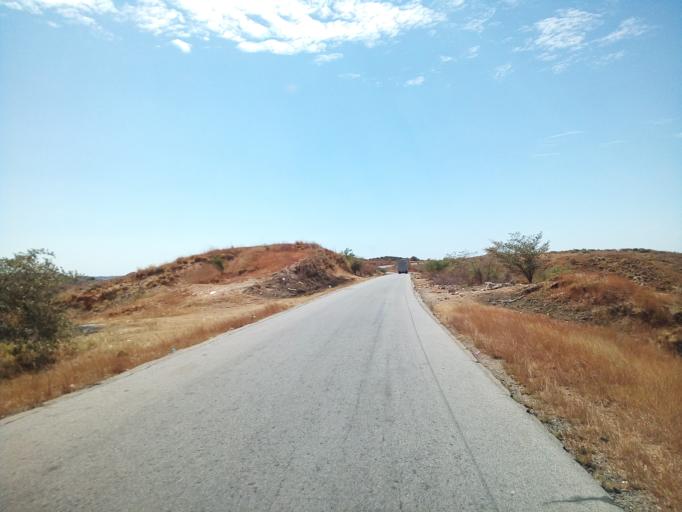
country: MG
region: Betsiboka
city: Maevatanana
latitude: -16.9480
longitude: 46.8547
